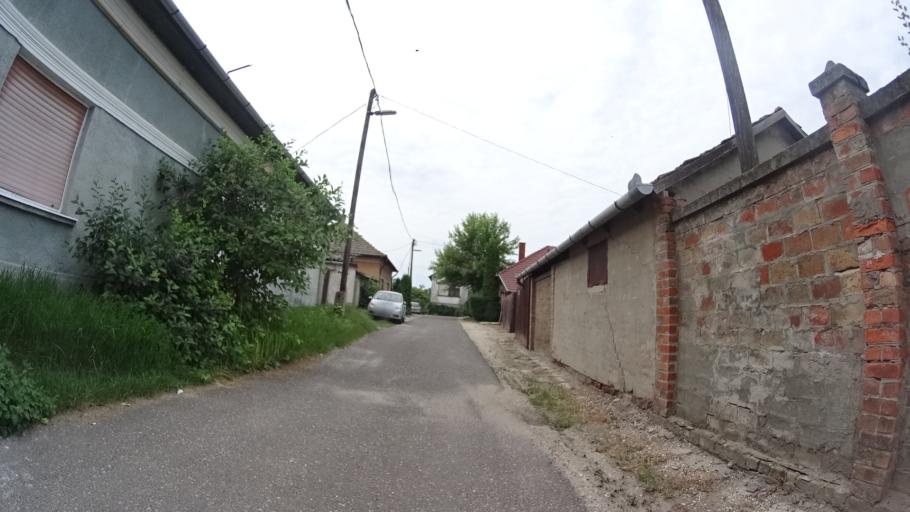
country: HU
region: Bacs-Kiskun
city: Tiszakecske
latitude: 46.9304
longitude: 20.0946
